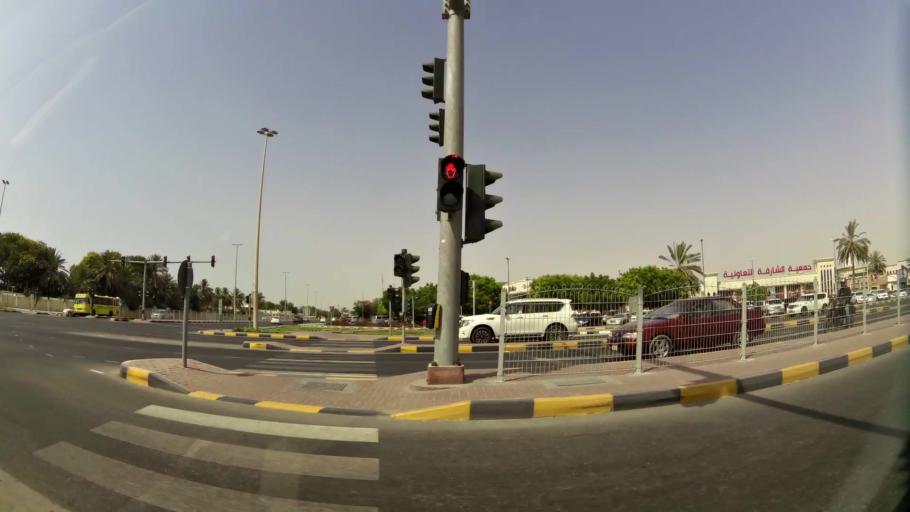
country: AE
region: Ash Shariqah
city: Sharjah
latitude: 25.3458
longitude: 55.4213
